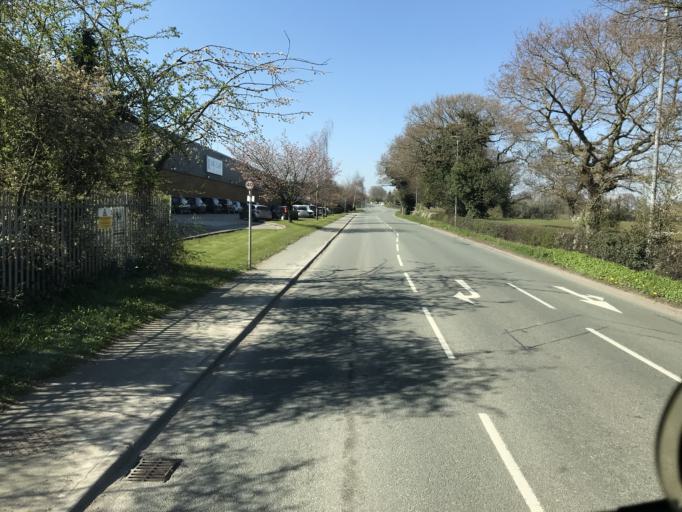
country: GB
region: Wales
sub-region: Wrexham
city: Gresford
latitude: 53.1000
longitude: -2.9986
